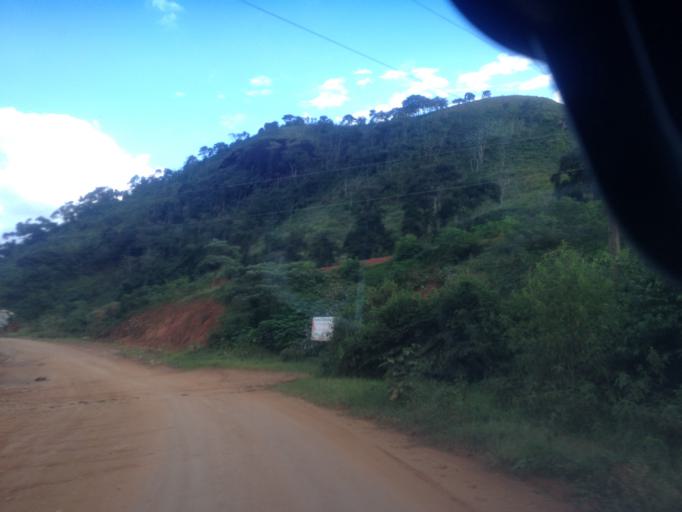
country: BR
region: Rio de Janeiro
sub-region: Quatis
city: Quatis
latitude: -22.2392
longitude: -44.2635
